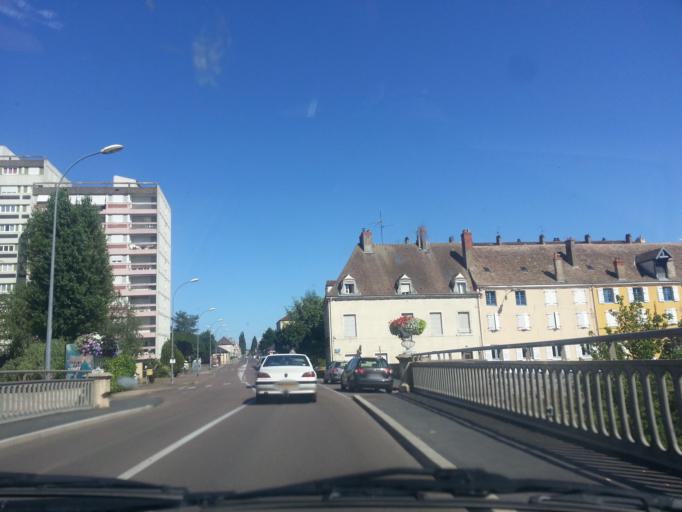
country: FR
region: Bourgogne
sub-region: Departement de Saone-et-Loire
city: Chalon-sur-Saone
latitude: 46.7792
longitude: 4.8631
